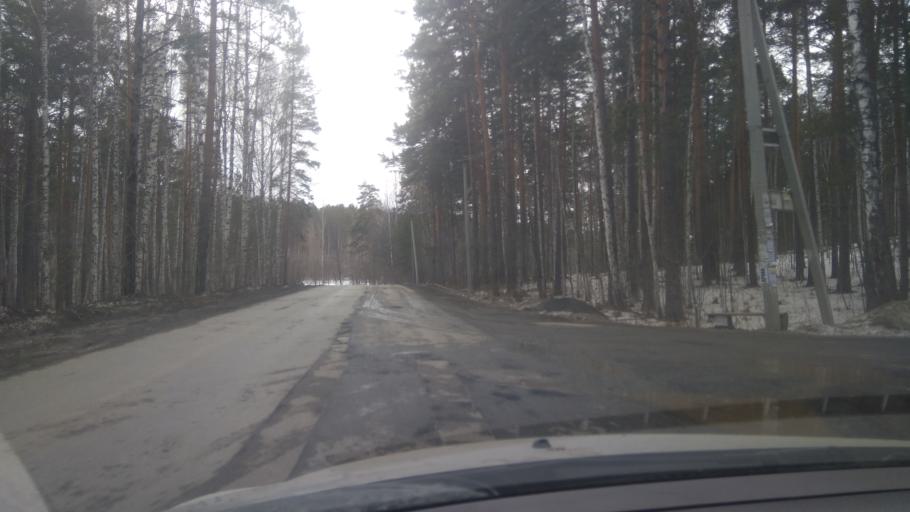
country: RU
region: Sverdlovsk
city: Severka
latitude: 56.8373
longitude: 60.3830
